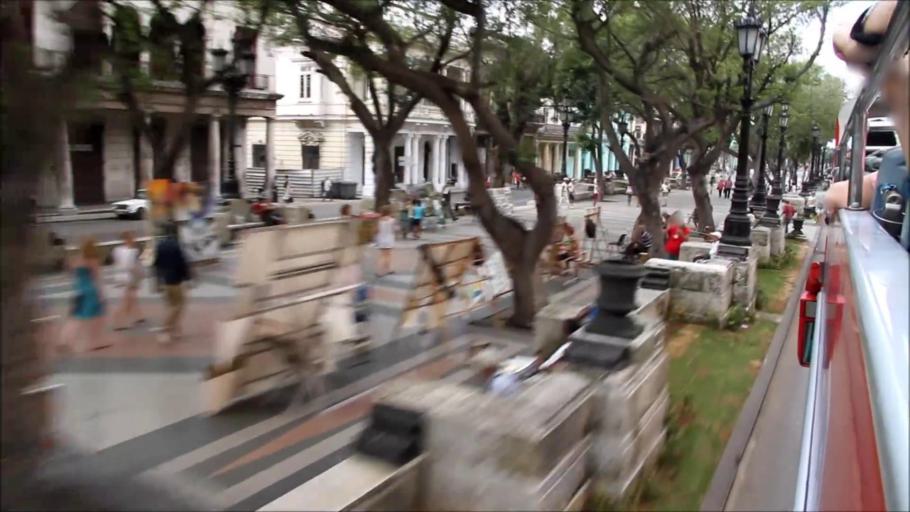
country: CU
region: La Habana
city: Centro Habana
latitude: 23.1403
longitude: -82.3589
